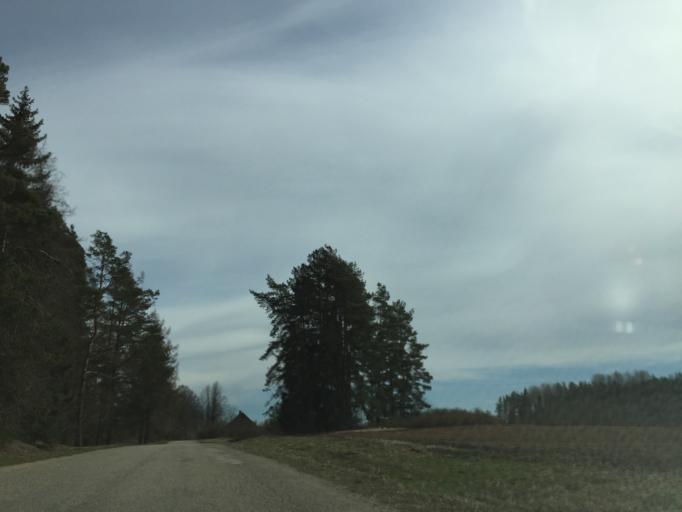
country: LV
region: Valkas Rajons
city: Valka
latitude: 57.8161
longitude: 25.9194
